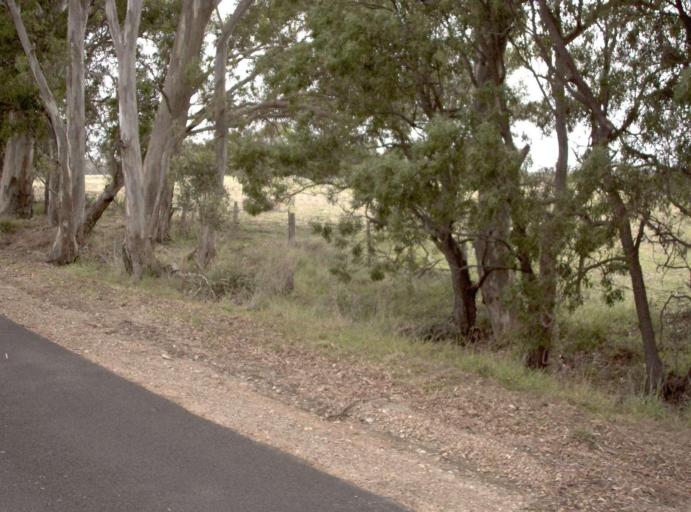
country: AU
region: Victoria
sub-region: Wellington
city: Sale
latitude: -37.8800
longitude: 147.0654
